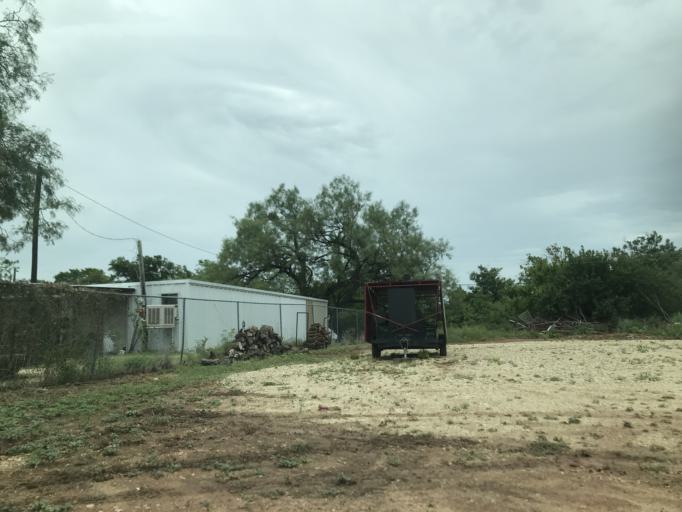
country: US
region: Texas
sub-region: Taylor County
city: Abilene
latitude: 32.4408
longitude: -99.7246
